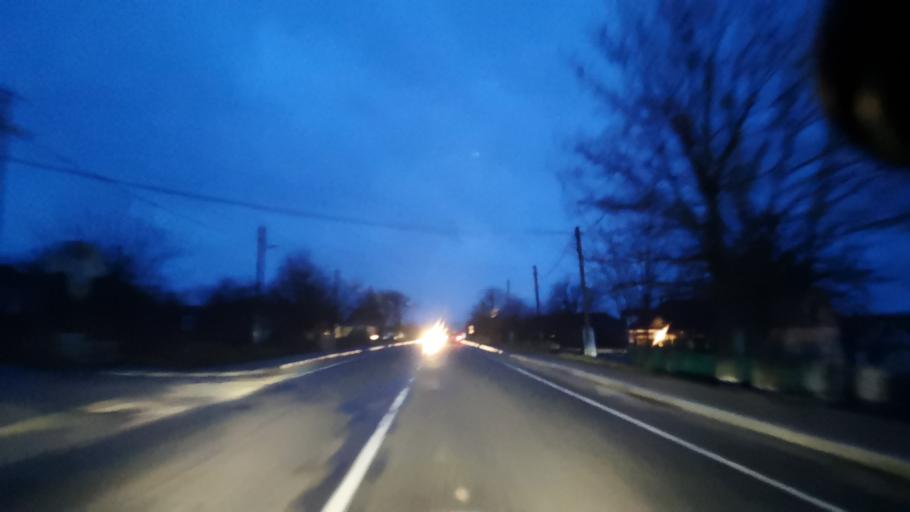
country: MD
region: Orhei
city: Orhei
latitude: 47.4428
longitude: 28.7947
